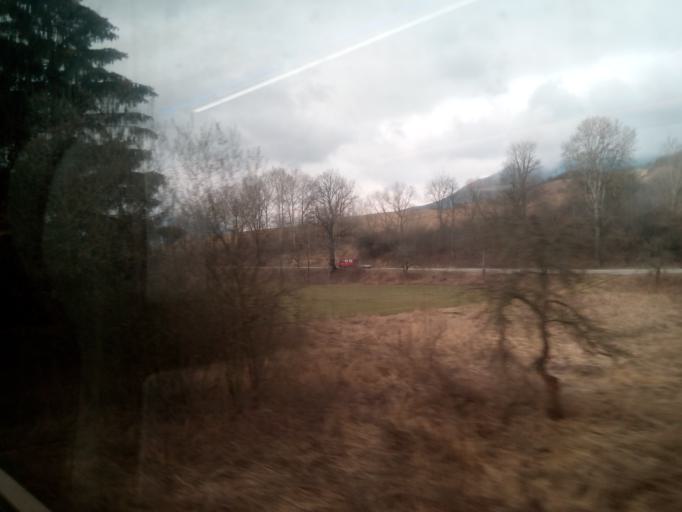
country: SK
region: Zilinsky
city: Ruzomberok
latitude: 49.0934
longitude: 19.3776
